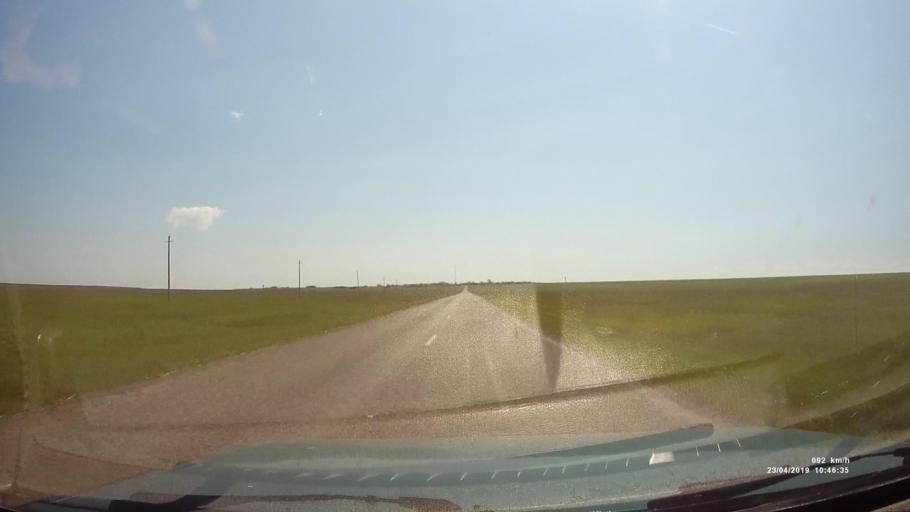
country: RU
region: Kalmykiya
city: Yashalta
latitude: 46.4418
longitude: 42.6934
